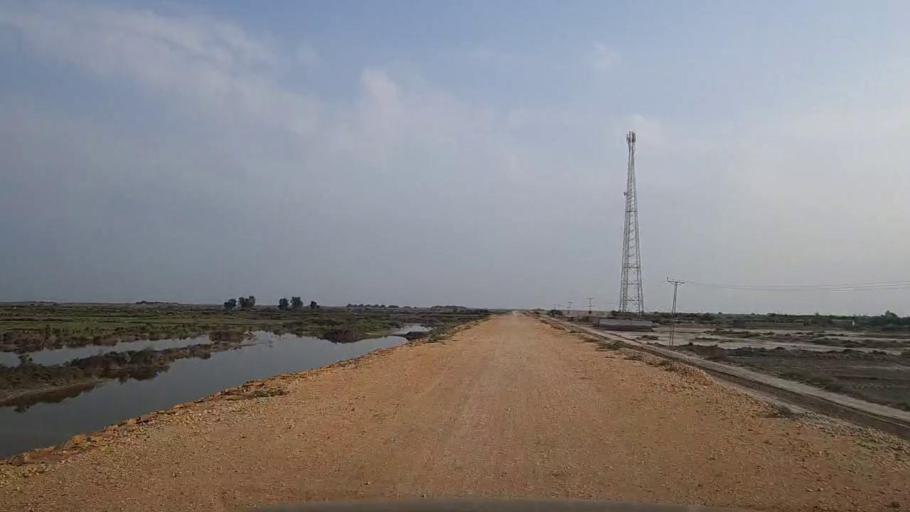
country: PK
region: Sindh
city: Thatta
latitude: 24.6181
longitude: 67.9614
